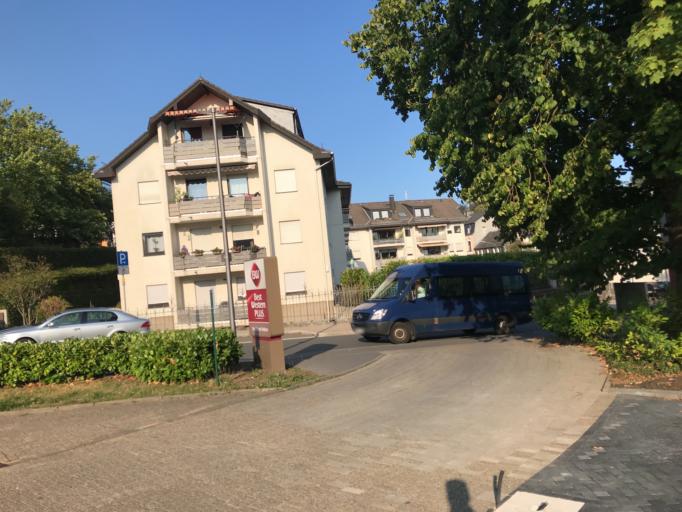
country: DE
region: North Rhine-Westphalia
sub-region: Regierungsbezirk Dusseldorf
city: Velbert
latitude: 51.3381
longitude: 7.0365
